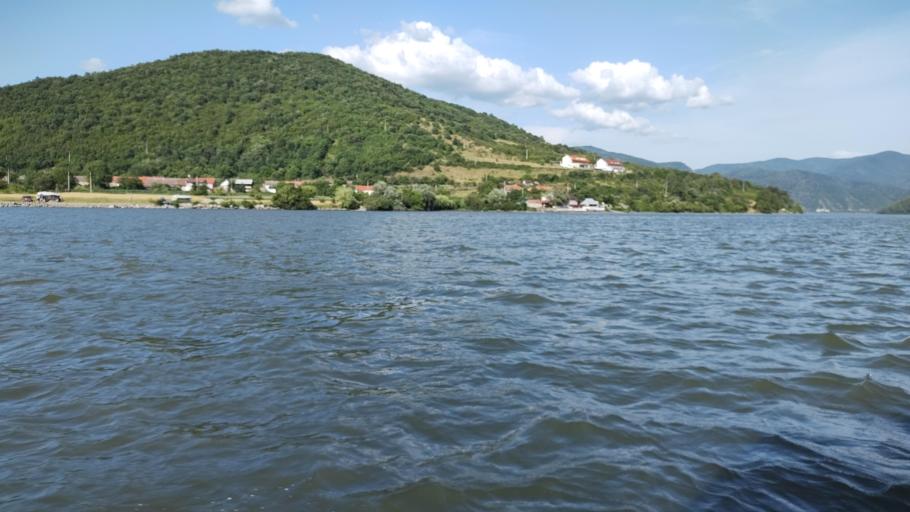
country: RO
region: Caras-Severin
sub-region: Comuna Berzasca
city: Berzasca
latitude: 44.6395
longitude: 21.9488
